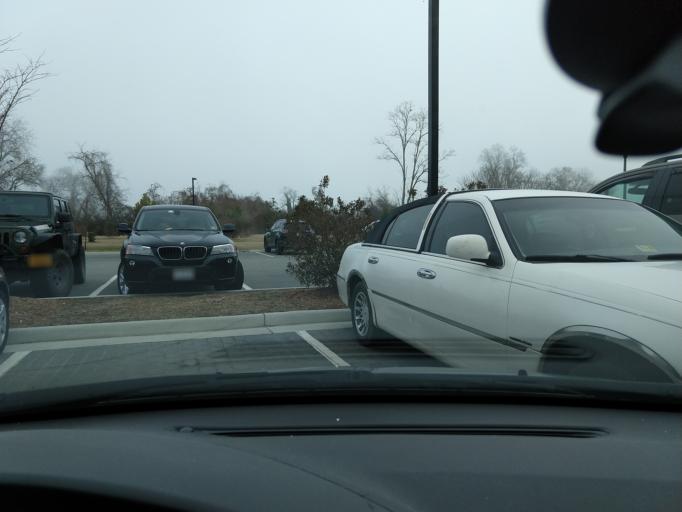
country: US
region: Virginia
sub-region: York County
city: Yorktown
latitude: 37.2389
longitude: -76.5176
